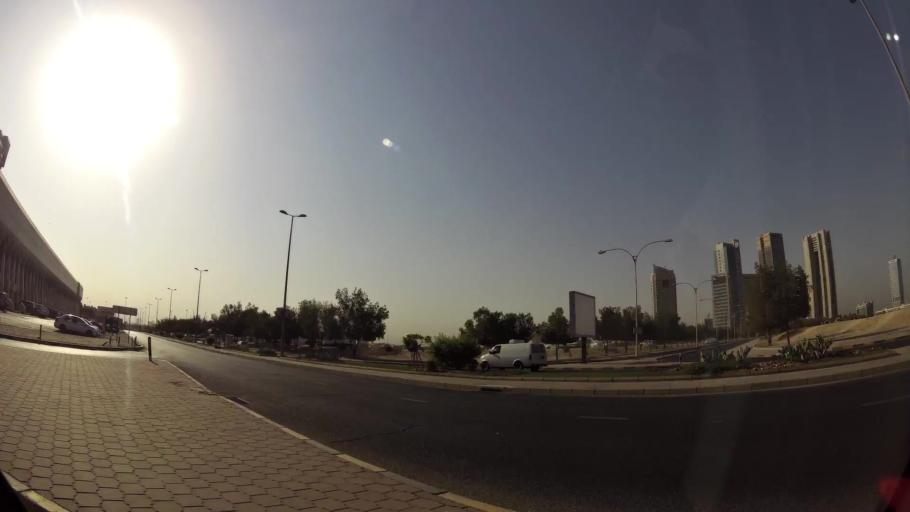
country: KW
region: Al Asimah
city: Kuwait City
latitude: 29.3694
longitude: 47.9844
